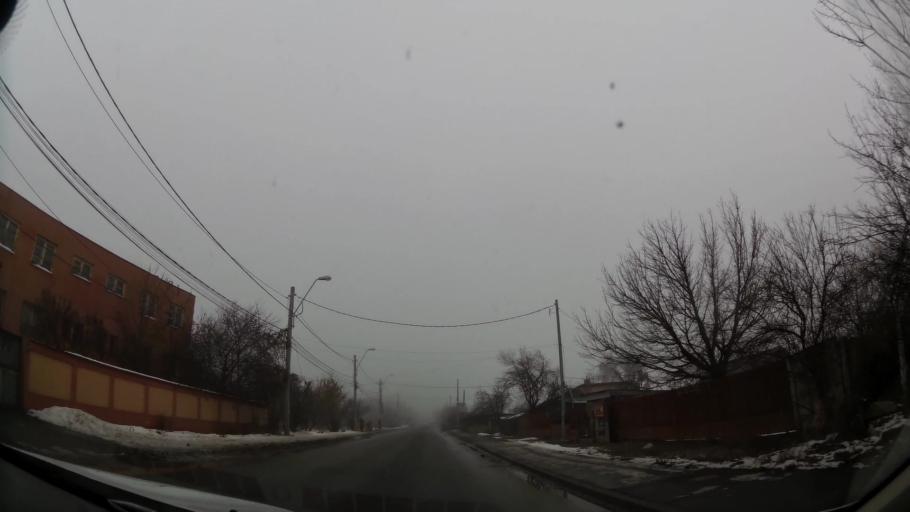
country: RO
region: Ilfov
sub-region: Comuna Chiajna
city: Rosu
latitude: 44.4742
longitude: 26.0142
